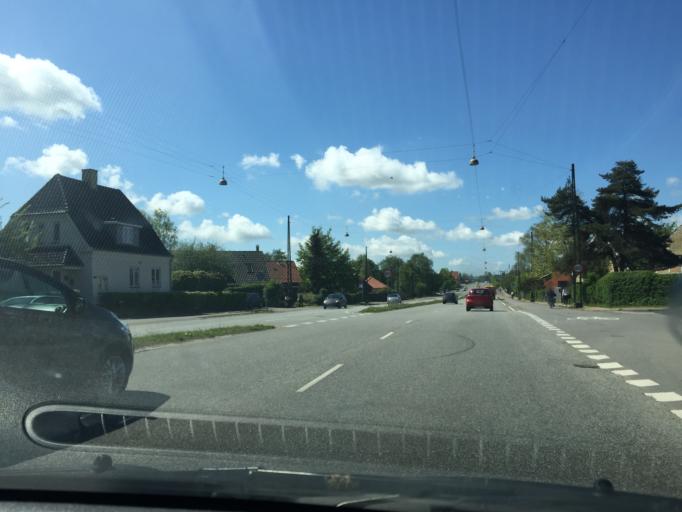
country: DK
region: Capital Region
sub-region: Kobenhavn
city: Vanlose
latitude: 55.6914
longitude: 12.4708
